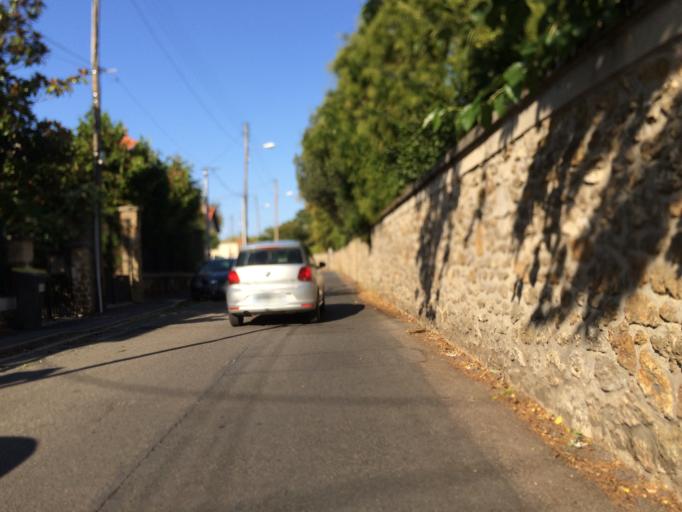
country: FR
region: Ile-de-France
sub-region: Departement de l'Essonne
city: Villiers-sur-Orge
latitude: 48.6605
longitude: 2.3070
